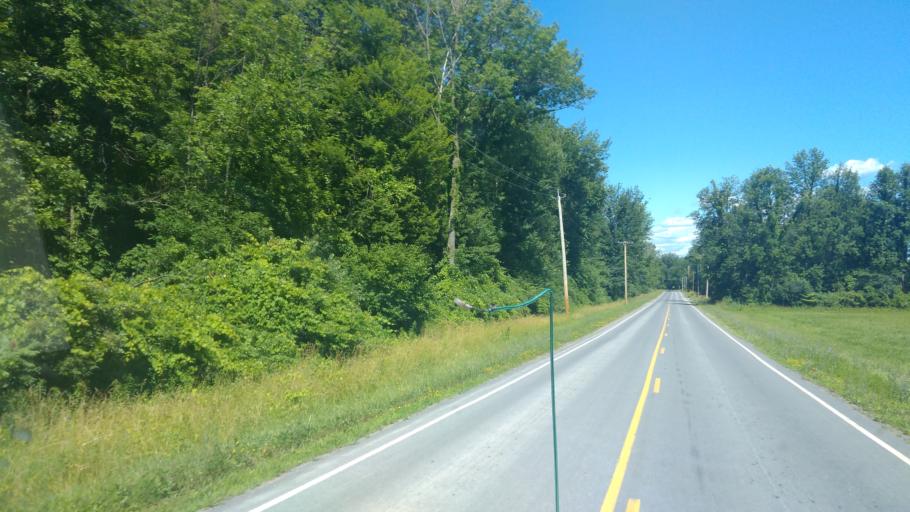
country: US
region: New York
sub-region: Wayne County
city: Sodus
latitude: 43.1803
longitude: -77.0185
